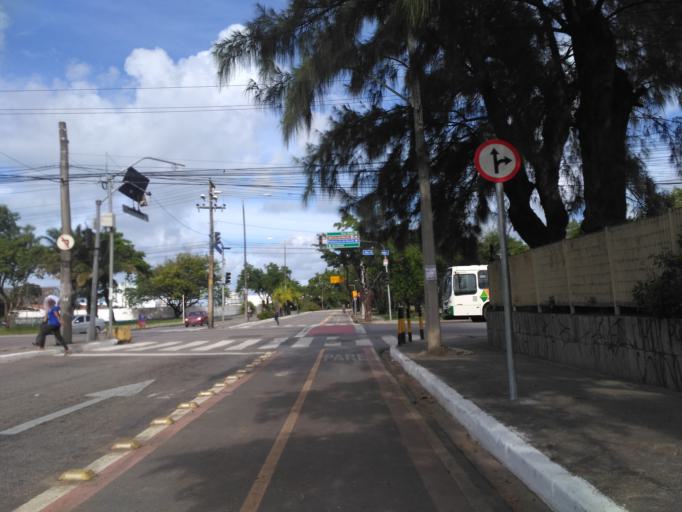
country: BR
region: Pernambuco
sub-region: Recife
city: Recife
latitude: -8.0446
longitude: -34.8752
